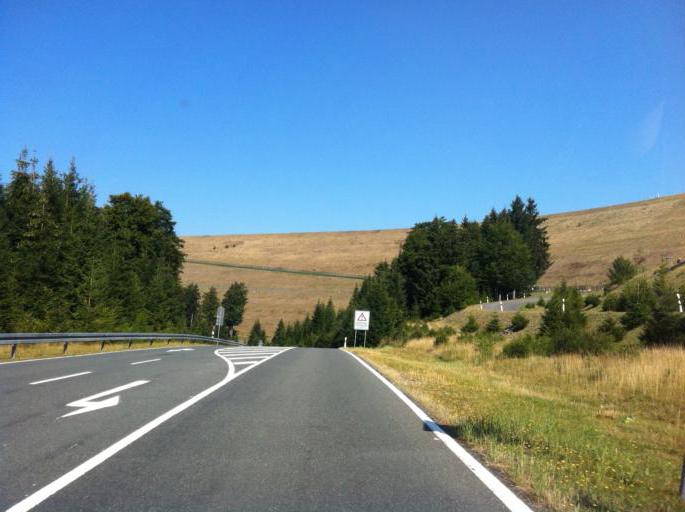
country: DE
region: Thuringia
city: Goldisthal
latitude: 50.5050
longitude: 11.0294
